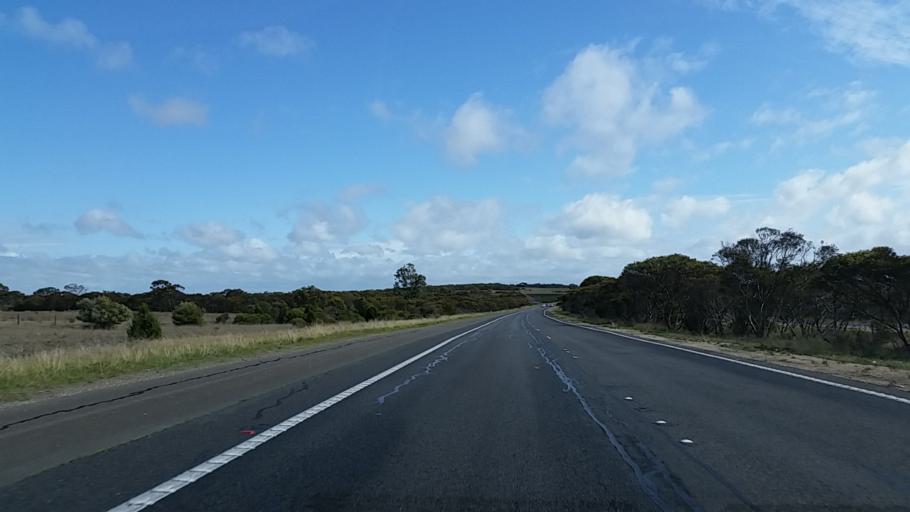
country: AU
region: South Australia
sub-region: Murray Bridge
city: Murray Bridge
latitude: -35.1524
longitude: 139.1990
